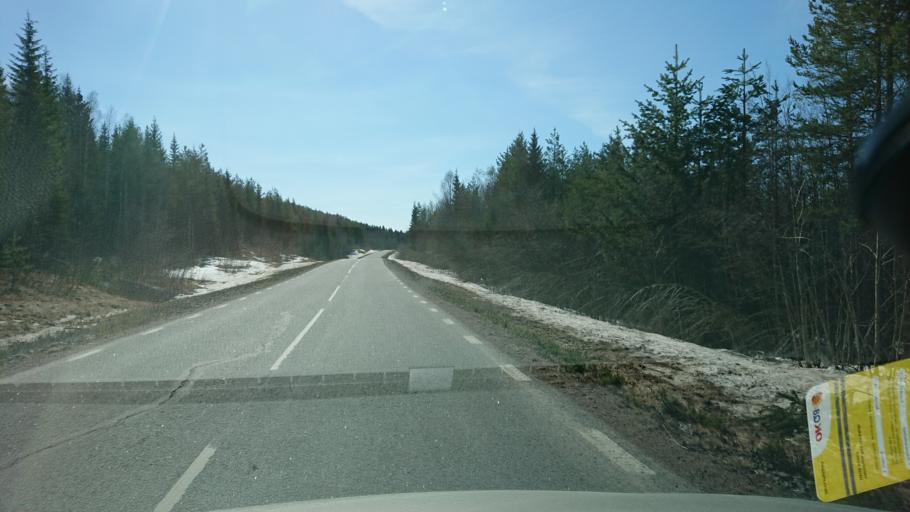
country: SE
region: Vaesternorrland
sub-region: Solleftea Kommun
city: As
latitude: 63.6814
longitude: 16.4321
